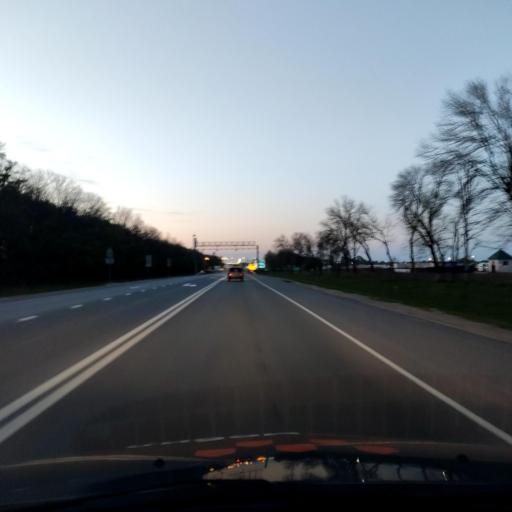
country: RU
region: Orjol
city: Zmiyevka
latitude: 52.7063
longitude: 36.3629
